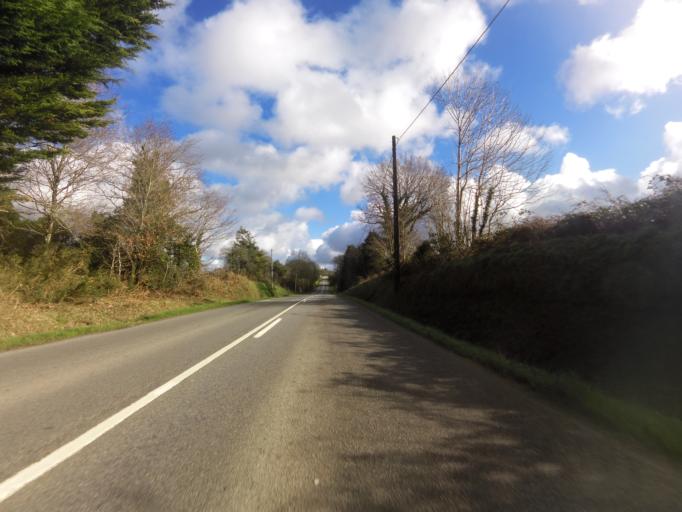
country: FR
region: Brittany
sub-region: Departement du Morbihan
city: Langonnet
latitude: 48.1440
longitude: -3.5104
